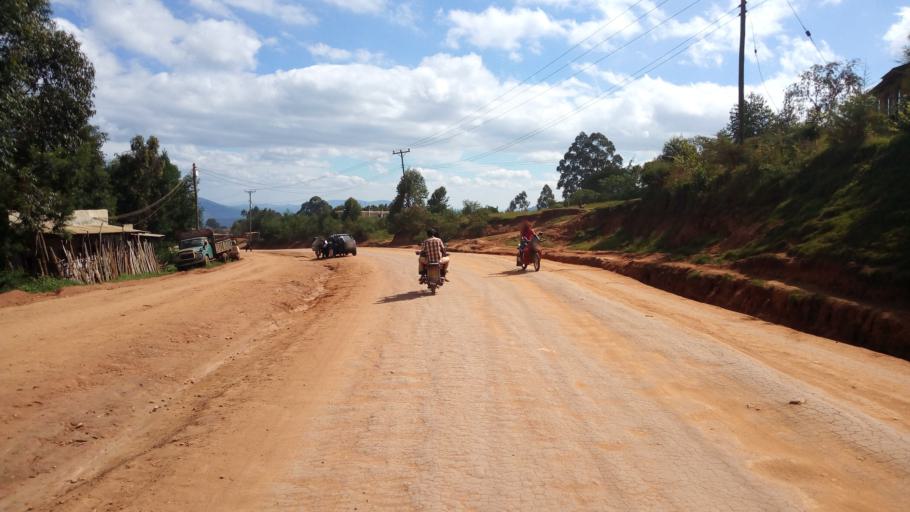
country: KE
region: Makueni
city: Wote
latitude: -1.6584
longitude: 37.4497
